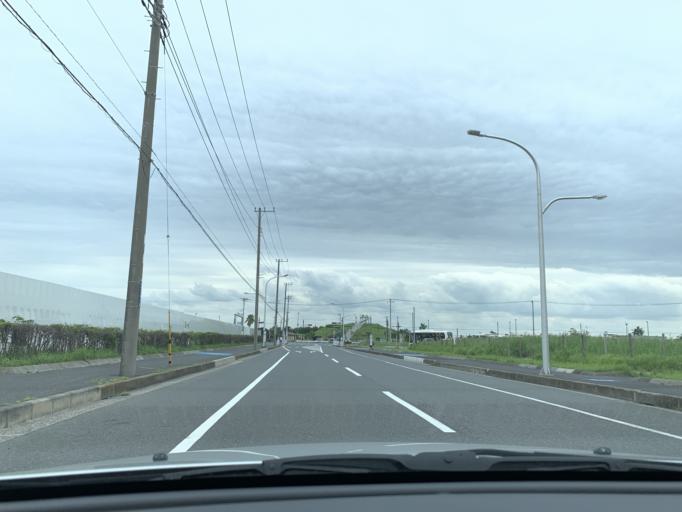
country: JP
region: Tokyo
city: Urayasu
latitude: 35.6342
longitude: 139.9198
